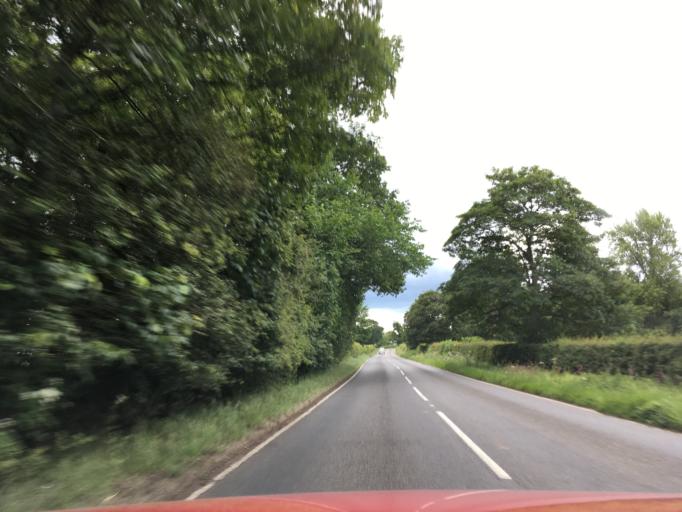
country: GB
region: England
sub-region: Central Bedfordshire
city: Potsgrove
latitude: 51.9713
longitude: -0.6425
